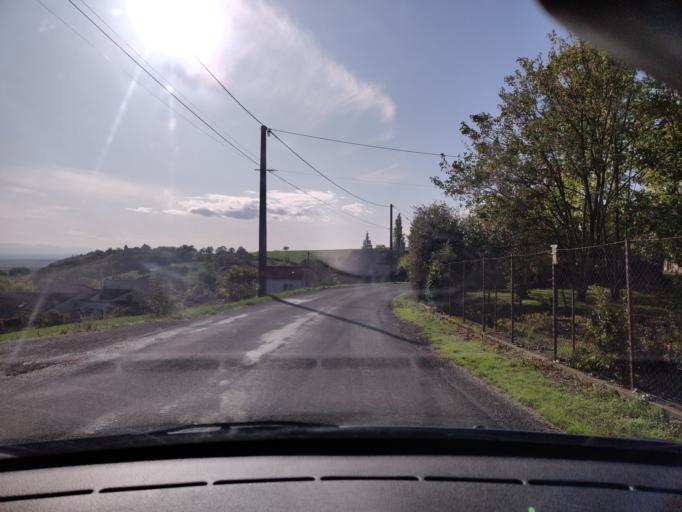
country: FR
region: Auvergne
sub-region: Departement du Puy-de-Dome
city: Aigueperse
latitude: 46.0339
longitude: 3.1653
